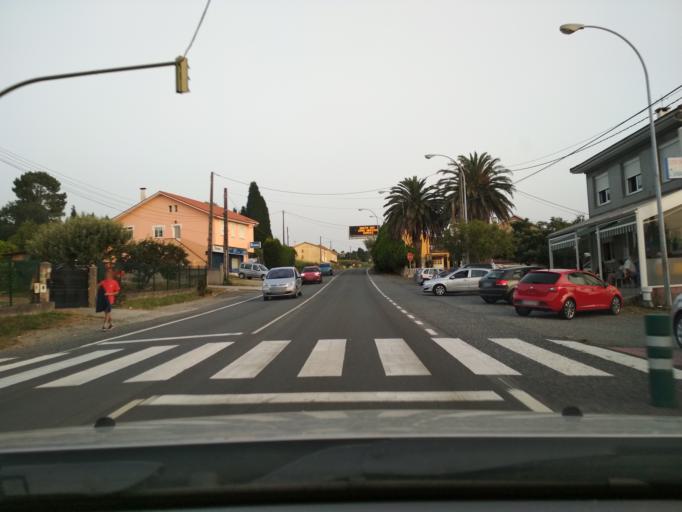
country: ES
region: Galicia
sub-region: Provincia da Coruna
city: Cambre
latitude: 43.2803
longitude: -8.3661
